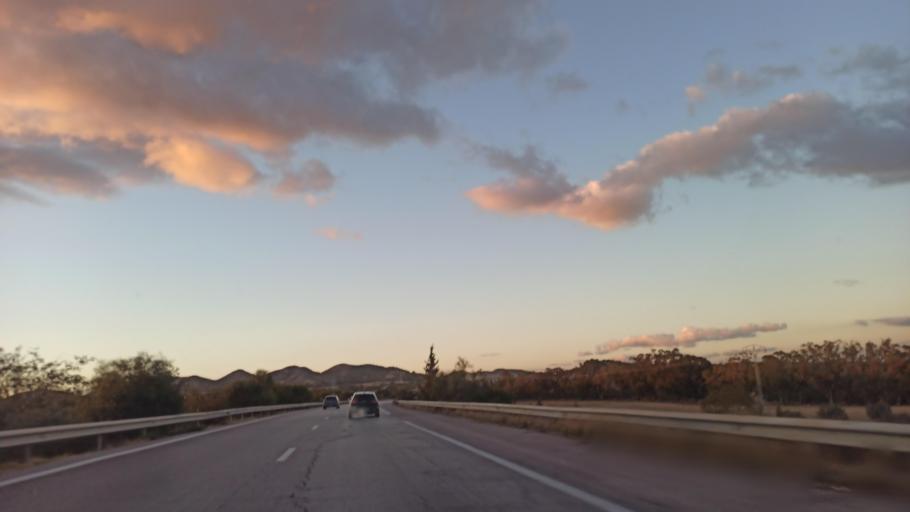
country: TN
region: Susah
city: Harqalah
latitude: 36.2139
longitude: 10.4223
